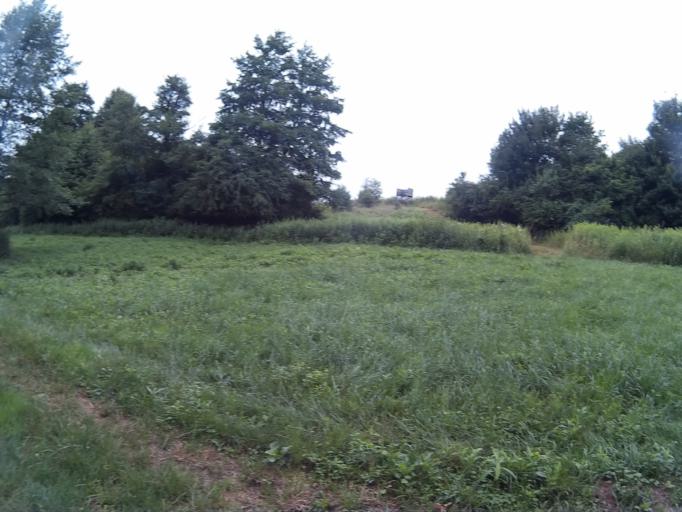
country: HU
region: Veszprem
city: Urkut
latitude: 47.1368
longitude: 17.6777
